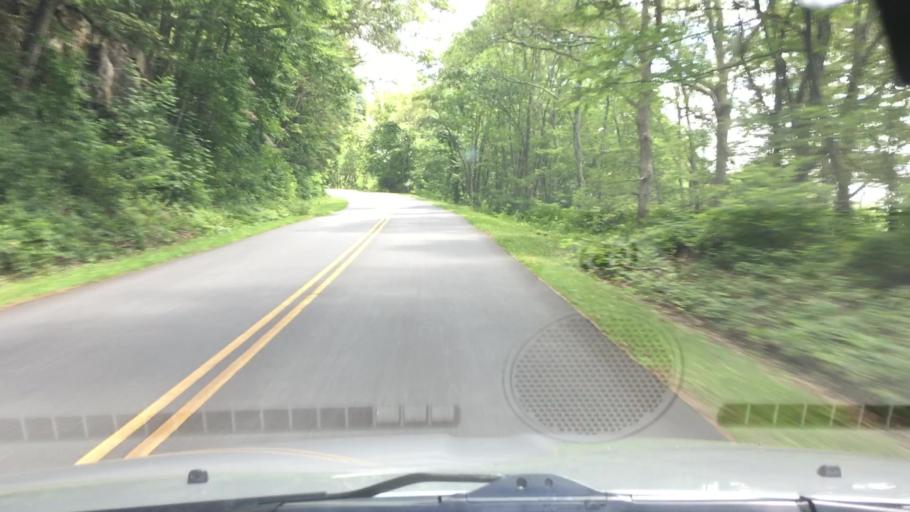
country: US
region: North Carolina
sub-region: Buncombe County
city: Swannanoa
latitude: 35.6756
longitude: -82.4387
